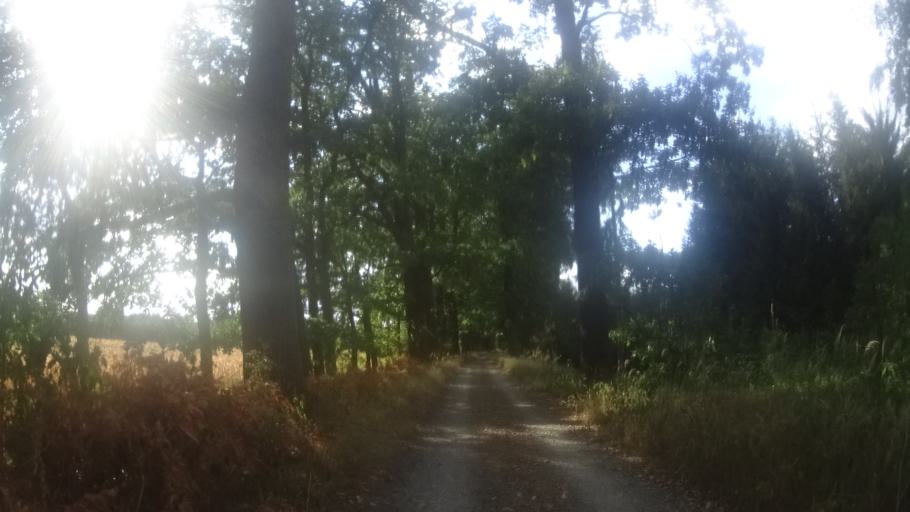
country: CZ
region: Kralovehradecky
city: Trebechovice pod Orebem
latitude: 50.1797
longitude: 16.0268
